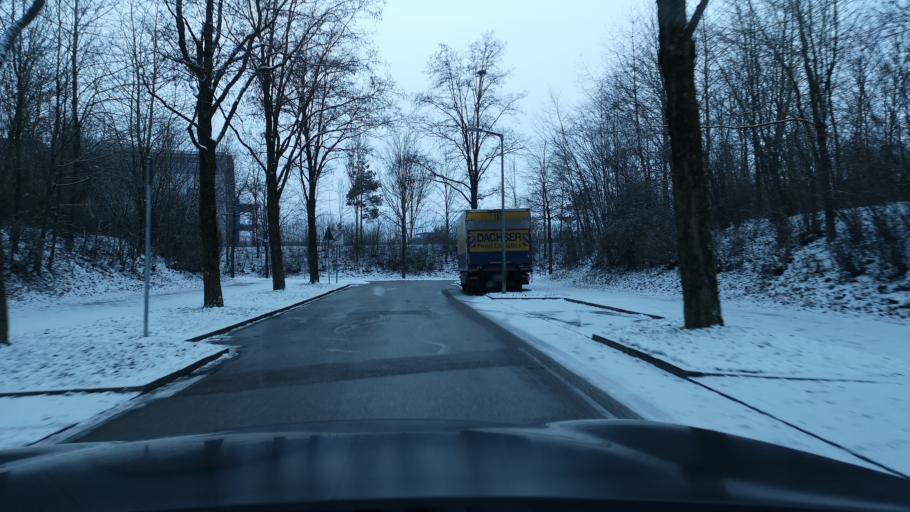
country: DE
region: Bavaria
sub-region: Upper Bavaria
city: Poing
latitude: 48.1734
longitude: 11.8007
